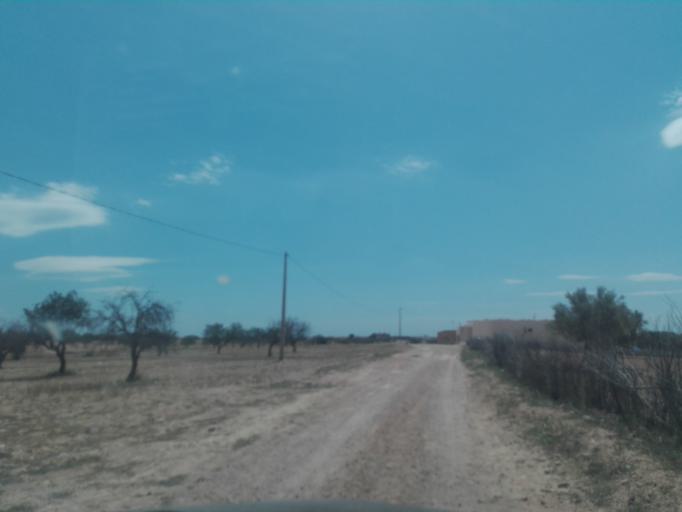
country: TN
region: Safaqis
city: Sfax
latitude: 34.6535
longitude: 10.5939
